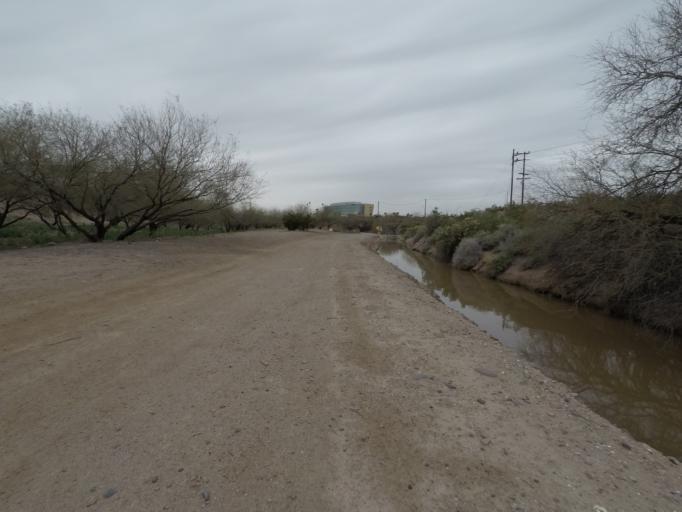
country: US
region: Arizona
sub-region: Maricopa County
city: Tempe Junction
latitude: 33.4360
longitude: -111.9389
